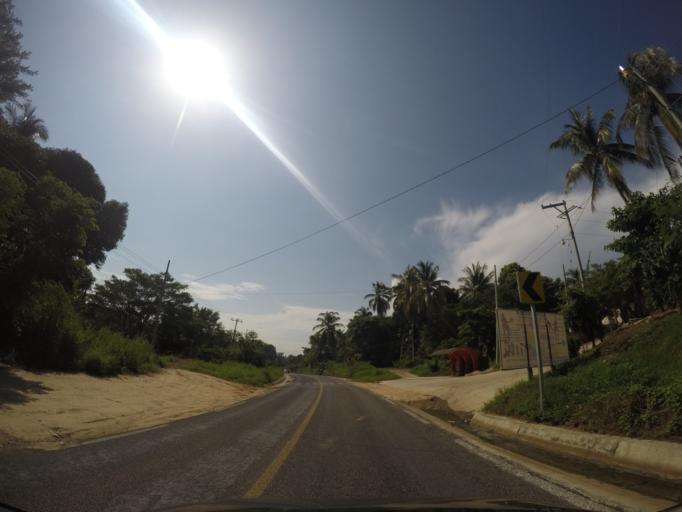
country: MX
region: Oaxaca
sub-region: San Pedro Mixtepec -Dto. 22 -
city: Puerto Escondido
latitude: 15.8832
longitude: -97.1080
